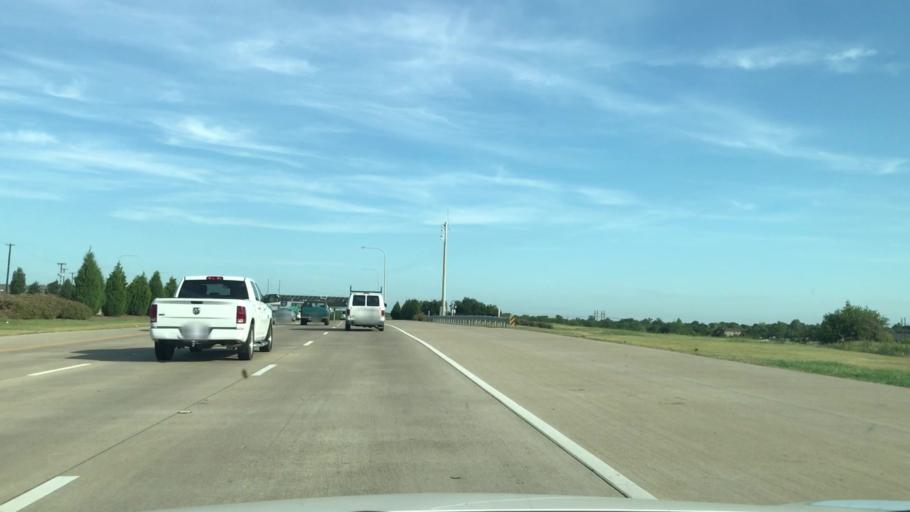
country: US
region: Texas
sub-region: Dallas County
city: Rowlett
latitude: 32.9429
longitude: -96.5569
